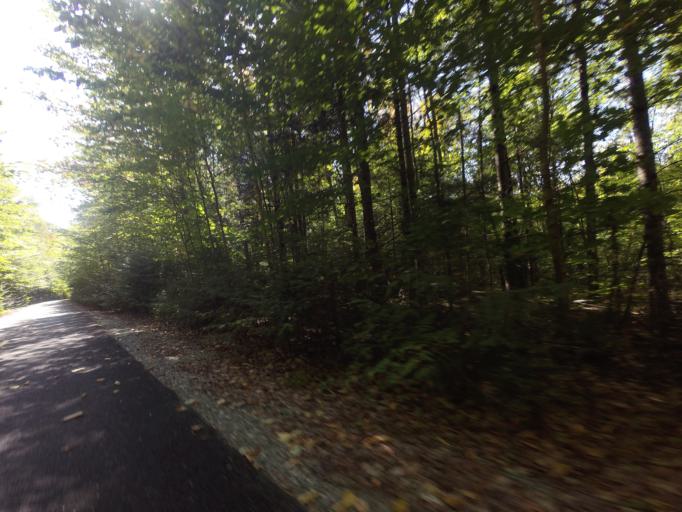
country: CA
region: Quebec
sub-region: Laurentides
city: Mont-Tremblant
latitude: 46.1240
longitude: -74.4991
